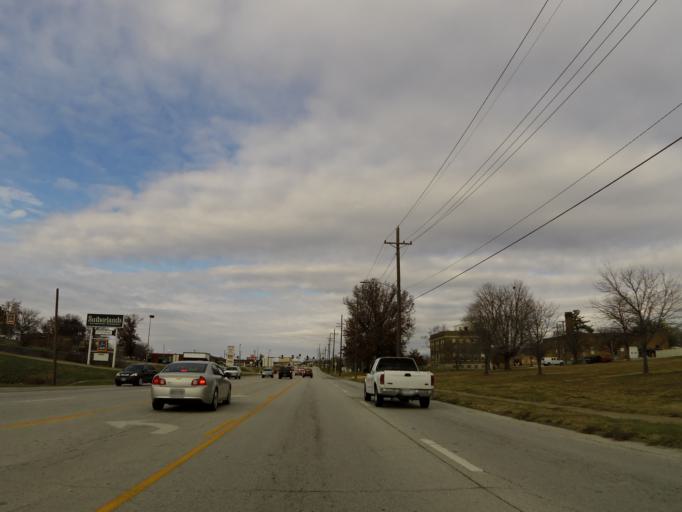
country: US
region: Missouri
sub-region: Marion County
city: Hannibal
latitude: 39.7211
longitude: -91.3919
